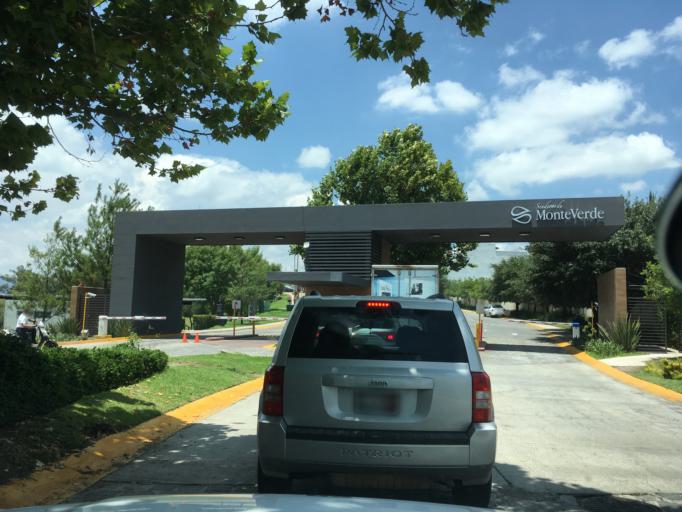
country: MX
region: Jalisco
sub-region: Tlajomulco de Zuniga
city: Lomas de San Agustin
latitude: 20.5127
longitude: -103.4875
